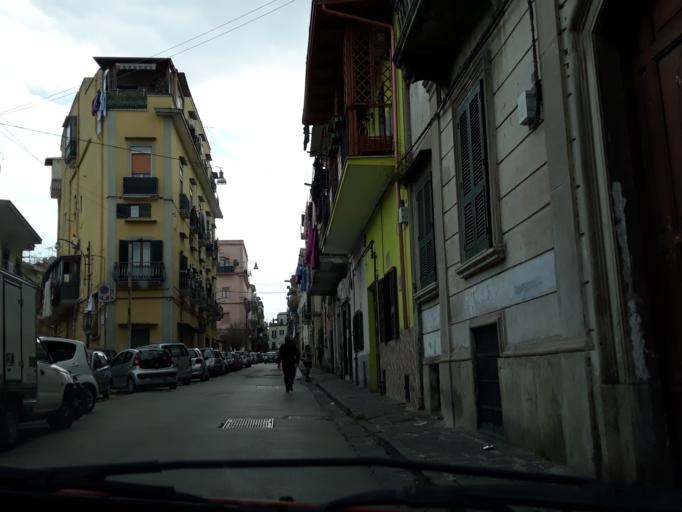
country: IT
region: Campania
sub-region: Provincia di Napoli
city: Mugnano di Napoli
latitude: 40.8883
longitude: 14.2302
